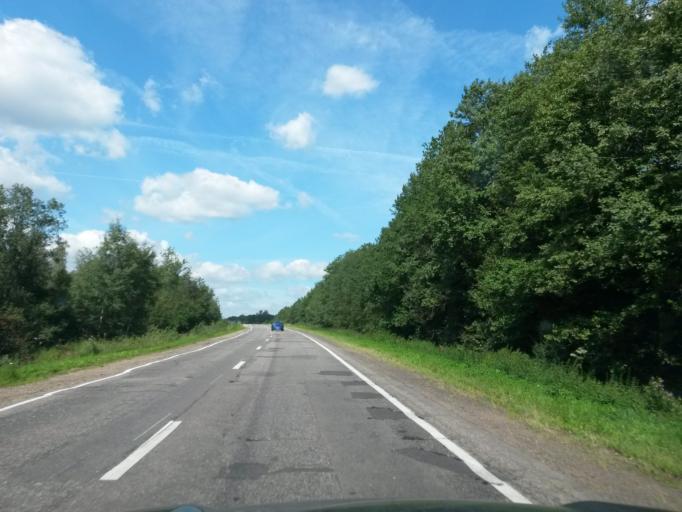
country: RU
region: Jaroslavl
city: Gavrilov-Yam
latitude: 57.4390
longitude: 39.9175
